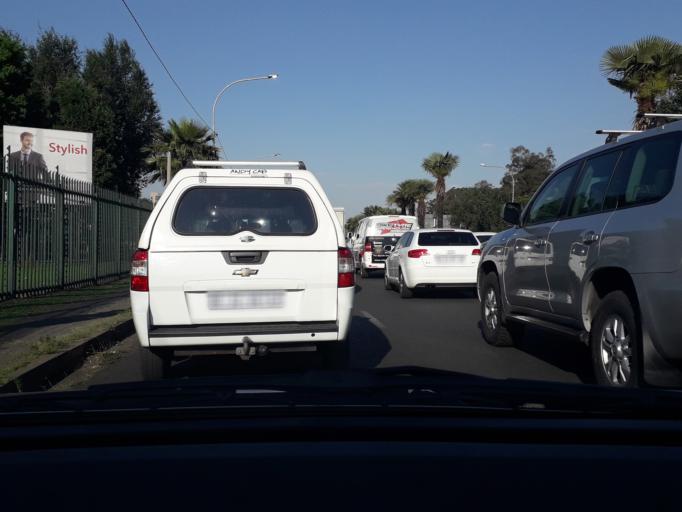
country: ZA
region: Gauteng
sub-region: City of Johannesburg Metropolitan Municipality
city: Johannesburg
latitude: -26.1831
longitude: 28.1080
